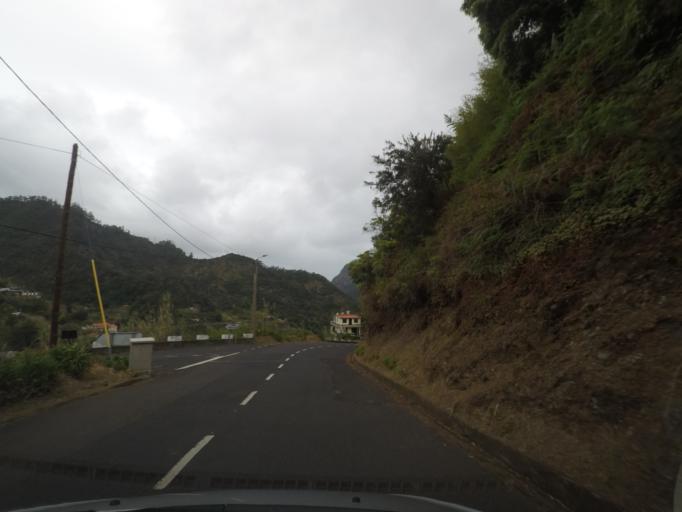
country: PT
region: Madeira
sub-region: Santana
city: Santana
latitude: 32.7540
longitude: -16.8374
